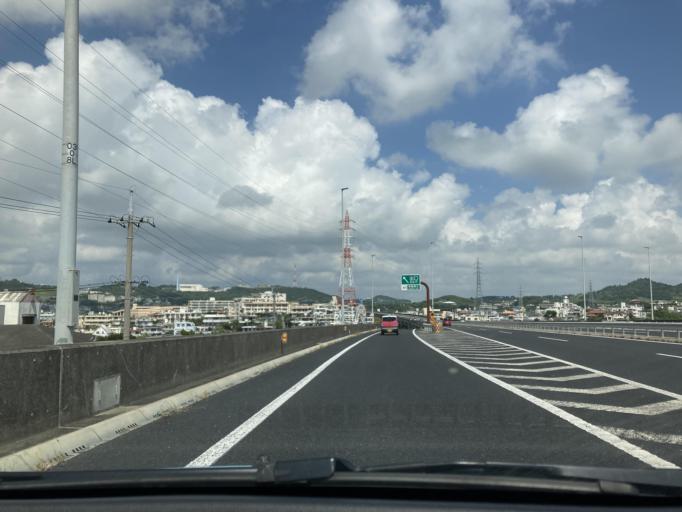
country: JP
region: Okinawa
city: Tomigusuku
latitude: 26.1942
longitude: 127.7394
